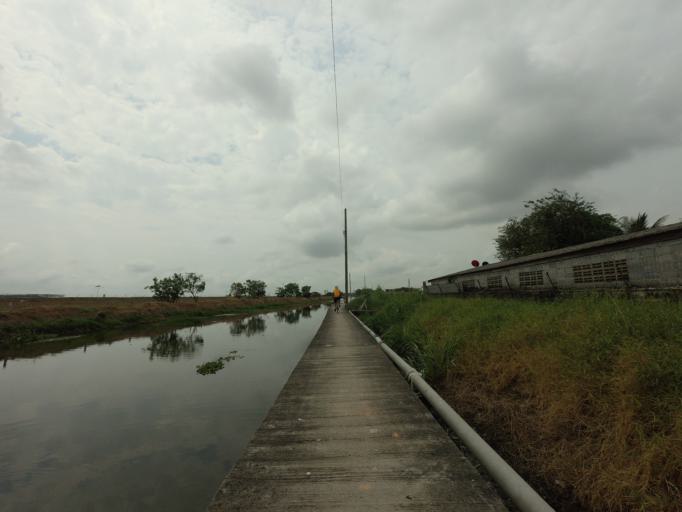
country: TH
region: Bangkok
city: Lat Krabang
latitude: 13.7112
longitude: 100.7412
